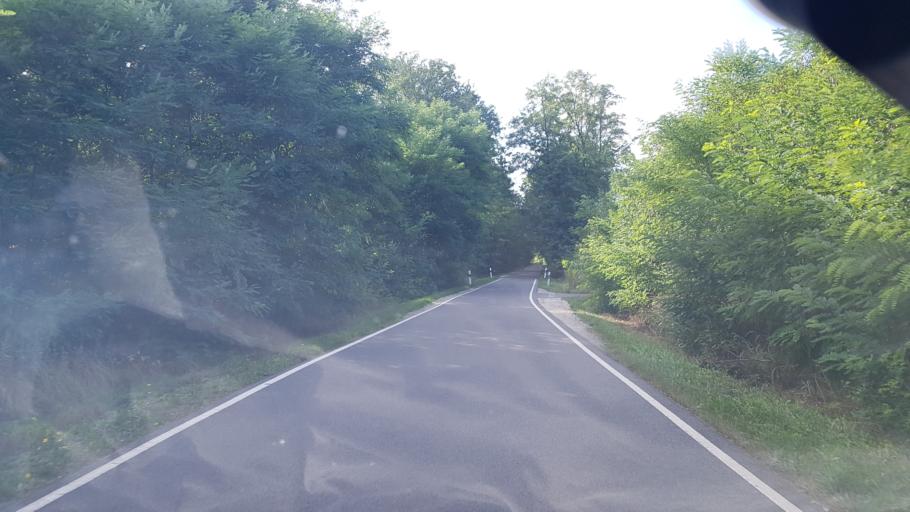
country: DE
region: Brandenburg
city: Spremberg
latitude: 51.5493
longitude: 14.3280
